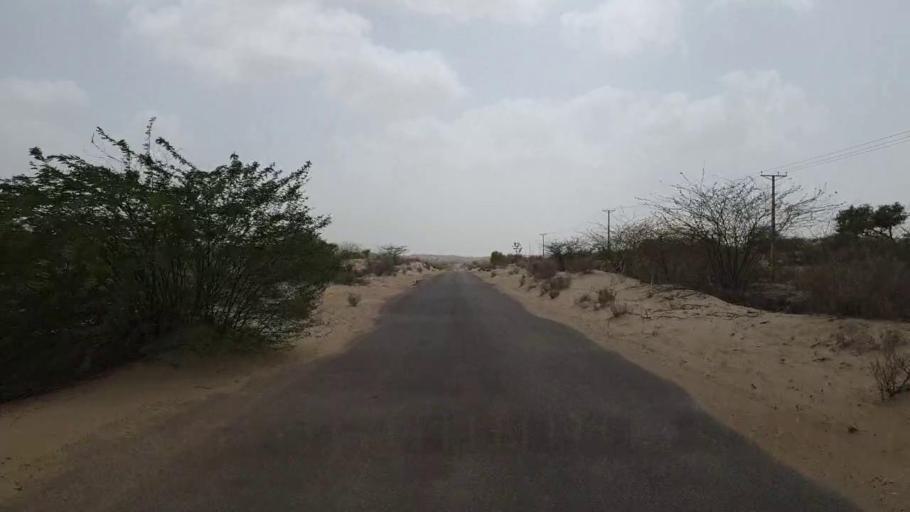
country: PK
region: Sindh
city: Diplo
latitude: 24.4006
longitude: 69.4697
